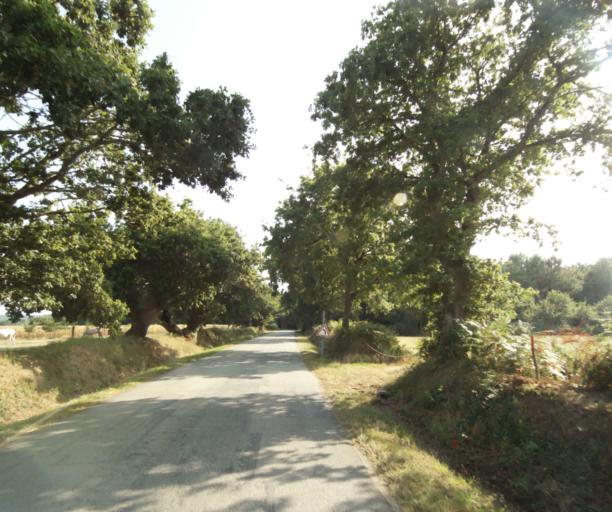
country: FR
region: Brittany
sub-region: Departement du Morbihan
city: Riantec
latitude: 47.7367
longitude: -3.2956
